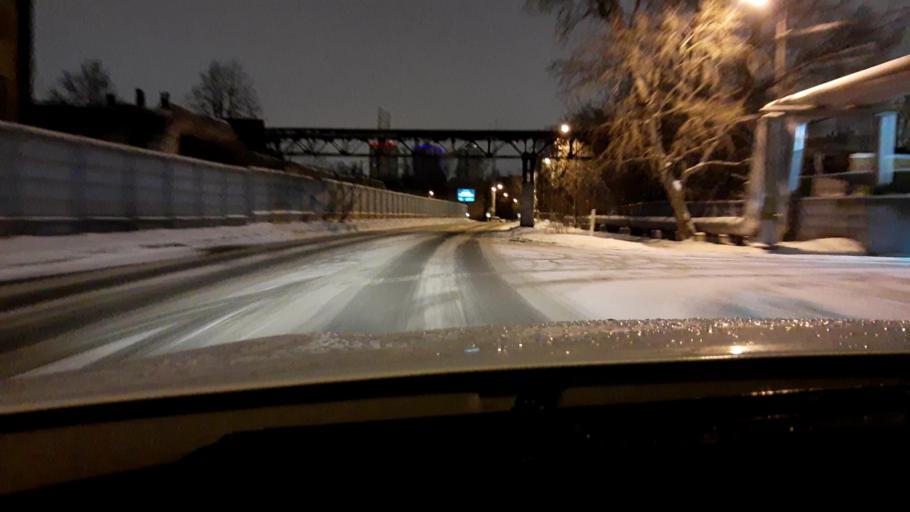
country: RU
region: Moscow
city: Khimki
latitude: 55.9012
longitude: 37.4437
